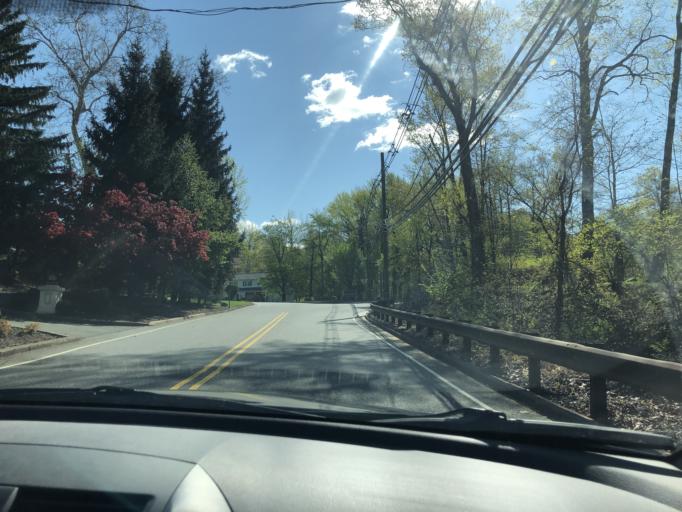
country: US
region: New Jersey
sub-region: Essex County
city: North Caldwell
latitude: 40.8690
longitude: -74.2661
